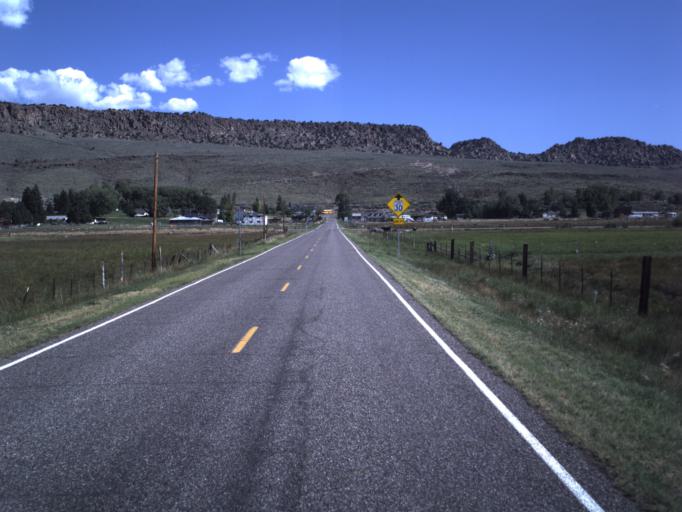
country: US
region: Utah
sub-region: Wayne County
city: Loa
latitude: 38.4528
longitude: -111.6158
